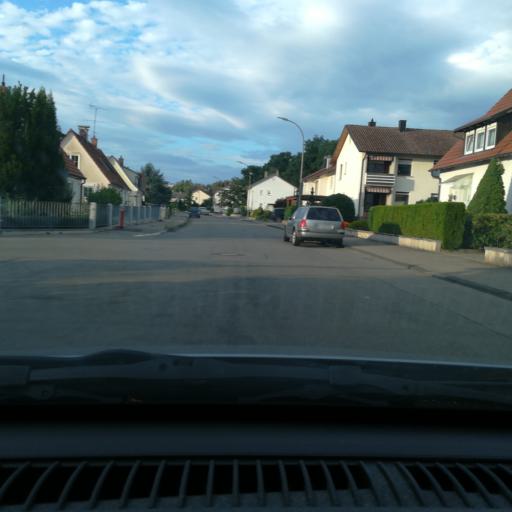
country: DE
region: Baden-Wuerttemberg
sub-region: Freiburg Region
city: Rielasingen-Worblingen
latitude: 47.7434
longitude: 8.8459
